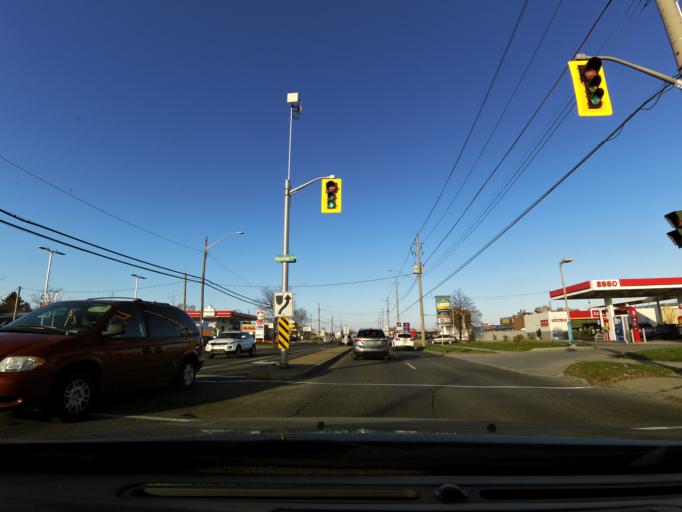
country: CA
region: Ontario
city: Hamilton
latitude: 43.2251
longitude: -79.8832
